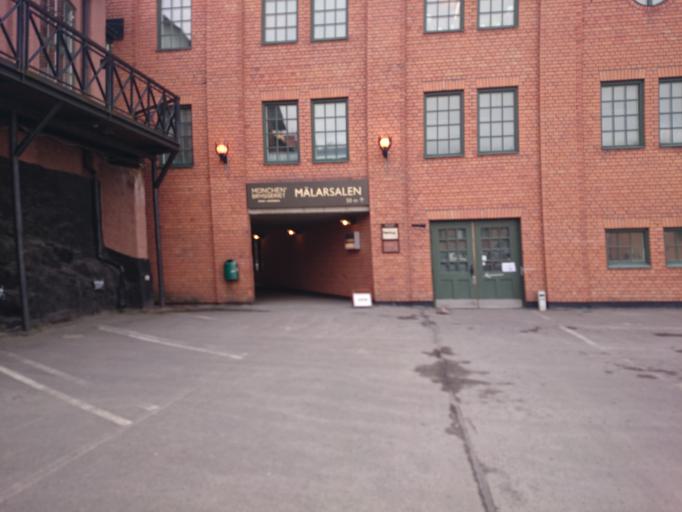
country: SE
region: Stockholm
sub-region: Stockholms Kommun
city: Stockholm
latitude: 59.3208
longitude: 18.0553
